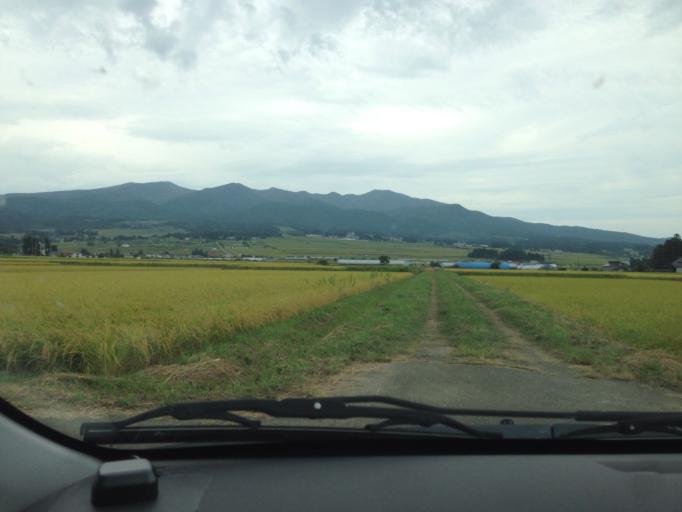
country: JP
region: Fukushima
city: Kitakata
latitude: 37.6324
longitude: 139.9075
